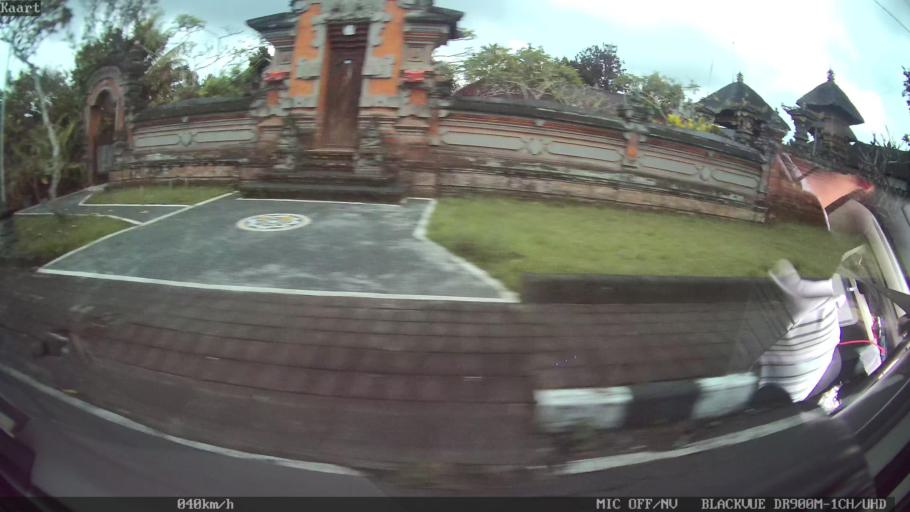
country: ID
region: Bali
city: Petang
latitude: -8.3979
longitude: 115.2187
